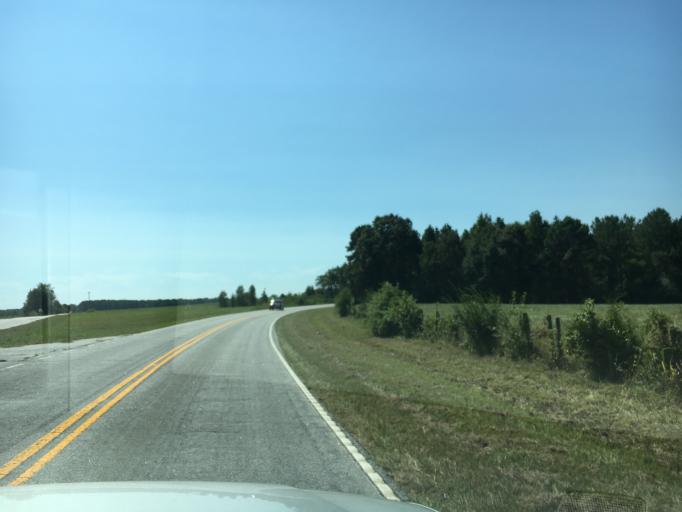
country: US
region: South Carolina
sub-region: Laurens County
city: Joanna
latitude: 34.3978
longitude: -81.8520
